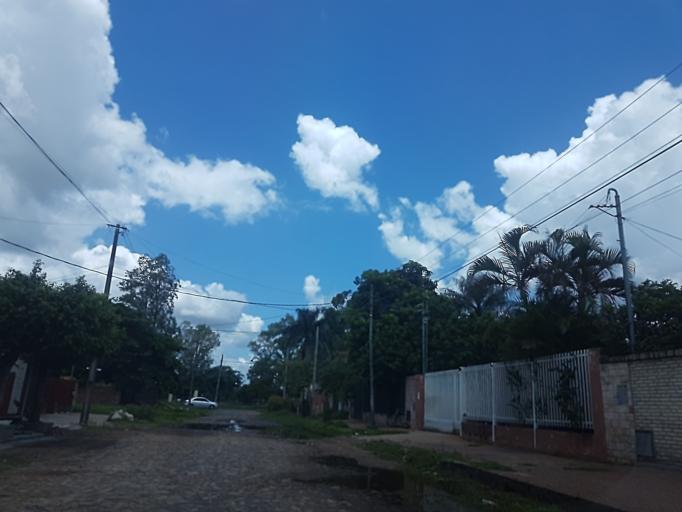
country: PY
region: Central
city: Colonia Mariano Roque Alonso
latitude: -25.2171
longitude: -57.5378
